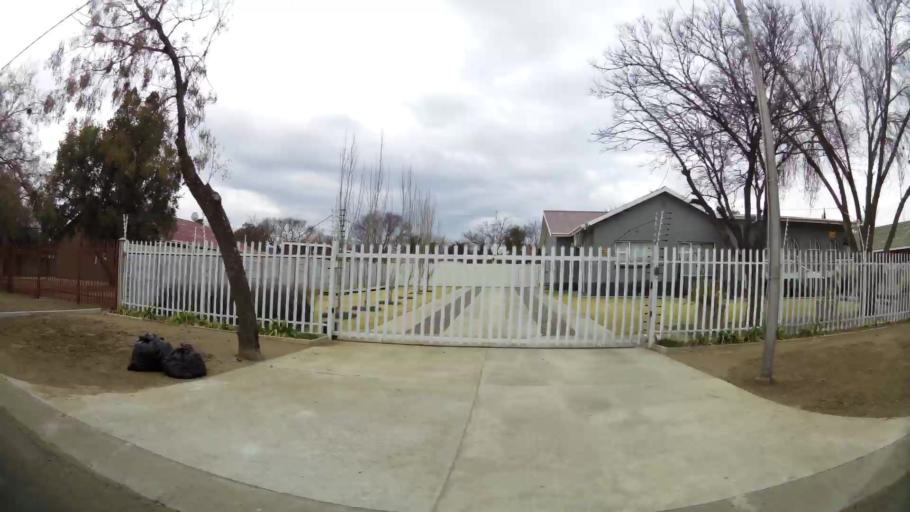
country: ZA
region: Orange Free State
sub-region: Fezile Dabi District Municipality
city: Kroonstad
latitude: -27.6820
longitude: 27.2296
